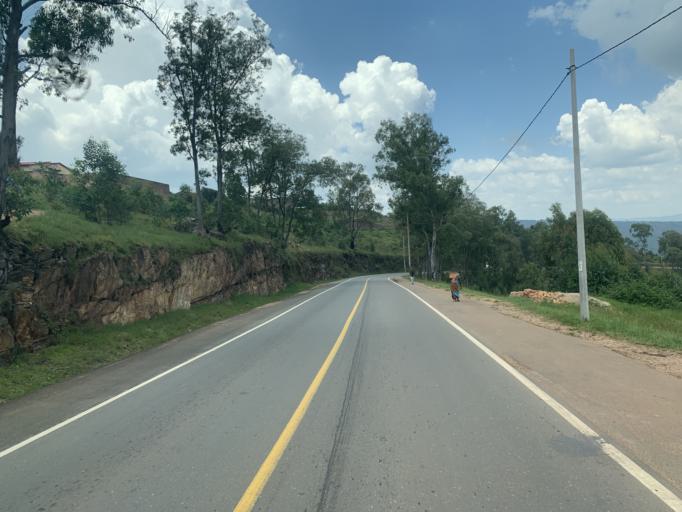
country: RW
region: Kigali
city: Kigali
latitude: -2.0021
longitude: 29.9053
